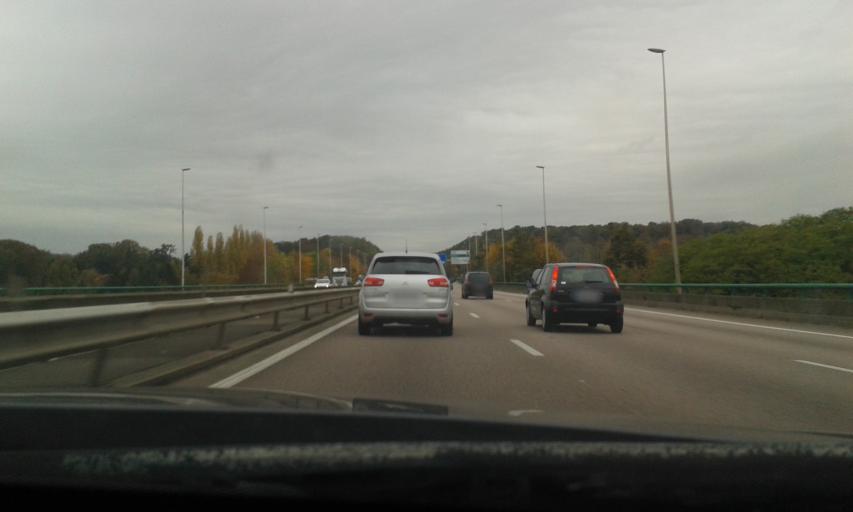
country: FR
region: Haute-Normandie
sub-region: Departement de la Seine-Maritime
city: Oissel
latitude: 49.3352
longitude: 1.0772
